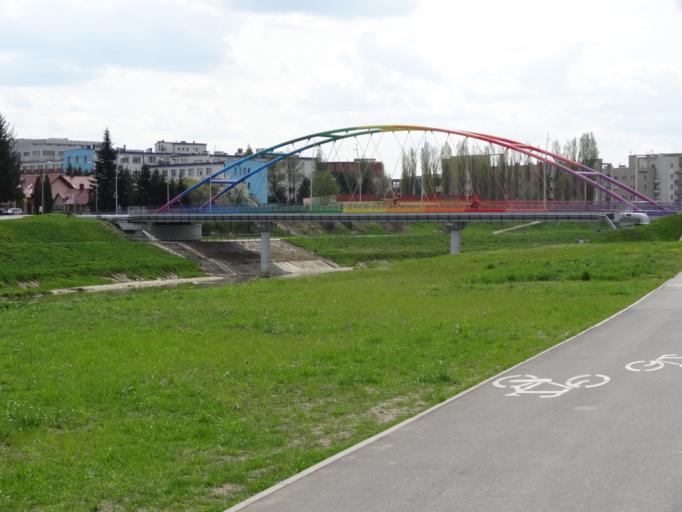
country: PL
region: Subcarpathian Voivodeship
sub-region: Rzeszow
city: Rzeszow
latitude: 50.0361
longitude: 22.0134
